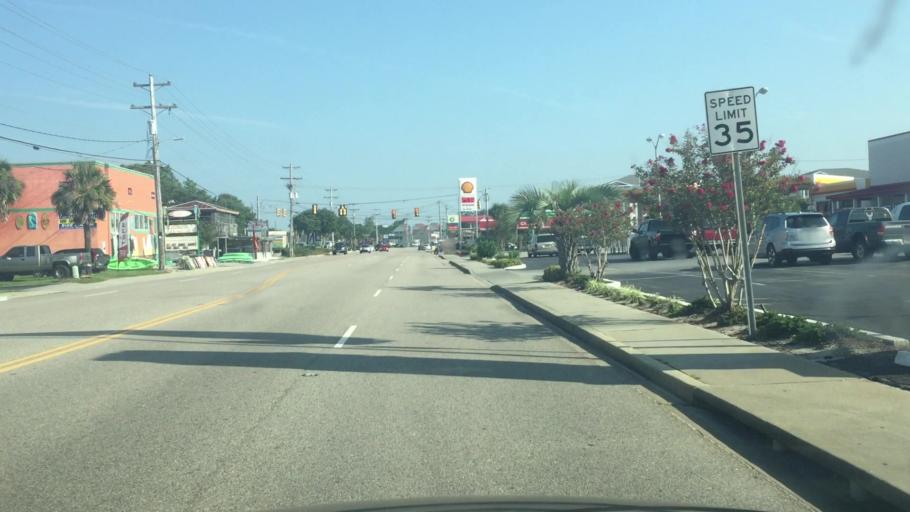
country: US
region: South Carolina
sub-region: Horry County
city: North Myrtle Beach
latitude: 33.8298
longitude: -78.6436
